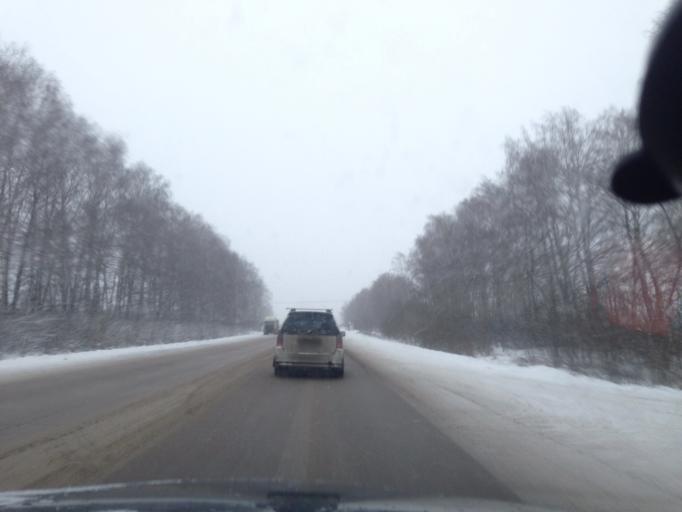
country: RU
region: Tula
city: Skuratovskiy
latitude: 54.1170
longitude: 37.7154
